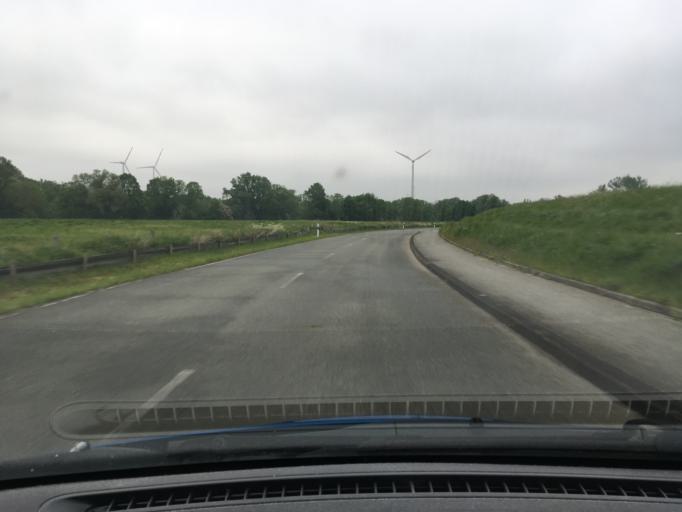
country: DE
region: Hamburg
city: Rothenburgsort
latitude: 53.4979
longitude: 10.0428
